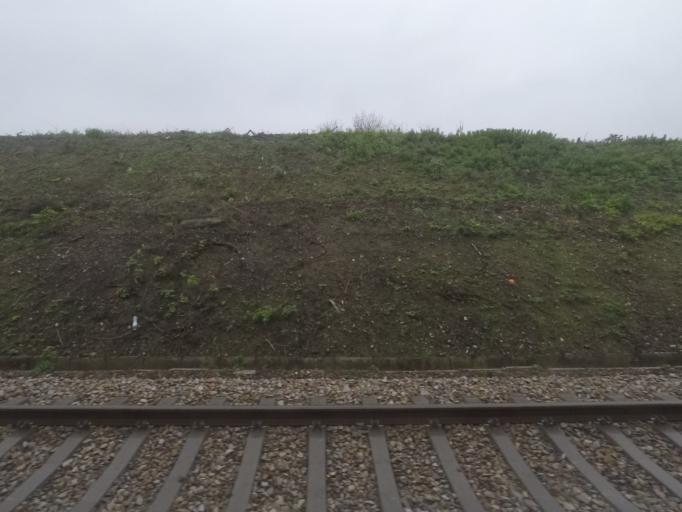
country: PL
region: Lesser Poland Voivodeship
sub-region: Powiat wielicki
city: Kokotow
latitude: 50.0919
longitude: 20.0462
